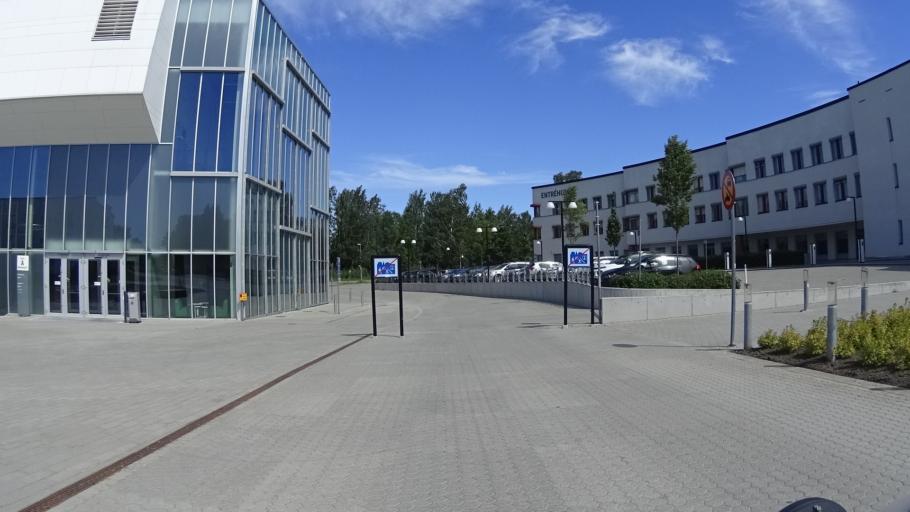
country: SE
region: OErebro
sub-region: Orebro Kommun
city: Orebro
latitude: 59.2543
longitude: 15.2450
